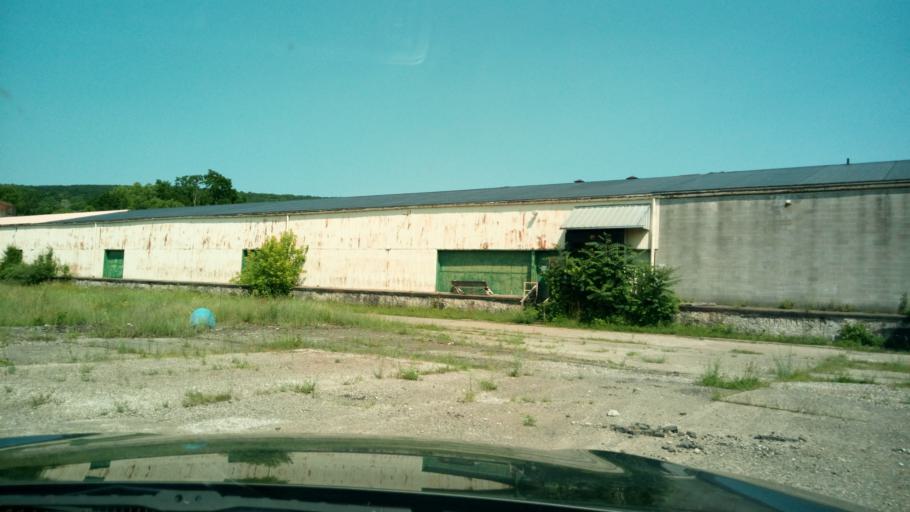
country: US
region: New York
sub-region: Chemung County
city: Elmira Heights
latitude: 42.1324
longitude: -76.8287
